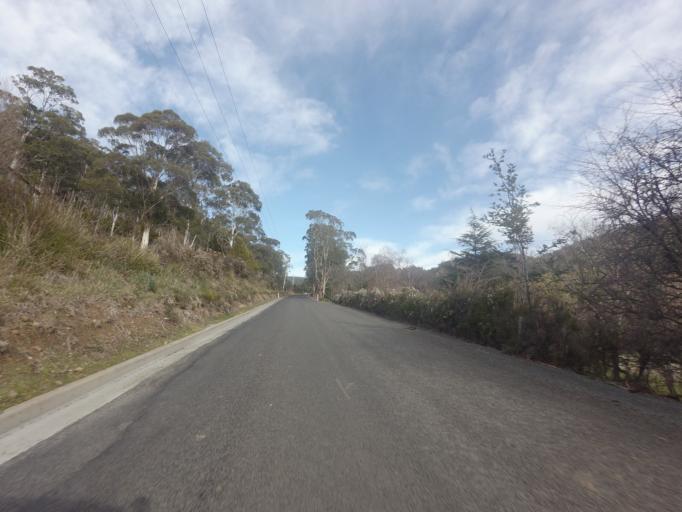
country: AU
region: Tasmania
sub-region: Kingborough
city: Margate
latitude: -42.9902
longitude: 147.1885
